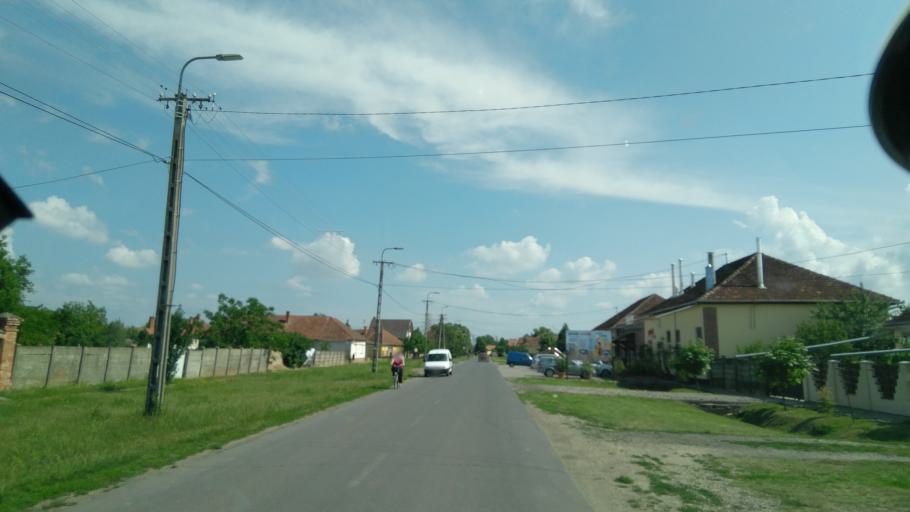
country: HU
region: Bekes
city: Doboz
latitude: 46.7320
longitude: 21.2394
